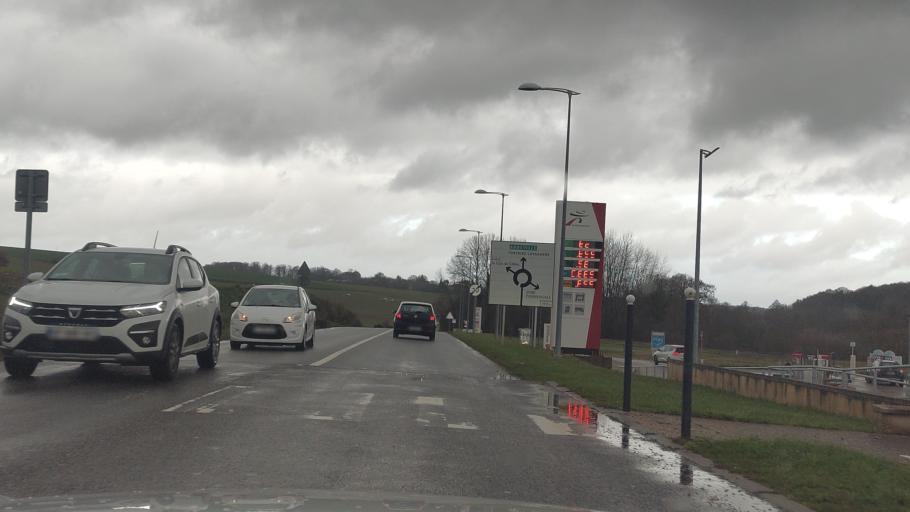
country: FR
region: Picardie
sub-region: Departement de l'Oise
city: Saint-Omer-en-Chaussee
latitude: 49.5812
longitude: 1.9538
